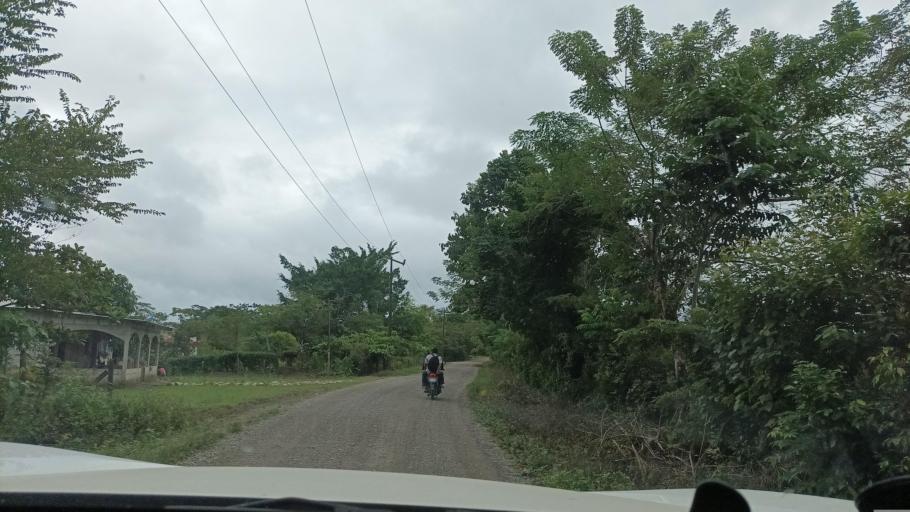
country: MX
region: Veracruz
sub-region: Uxpanapa
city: Poblado 10
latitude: 17.4108
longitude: -94.4166
